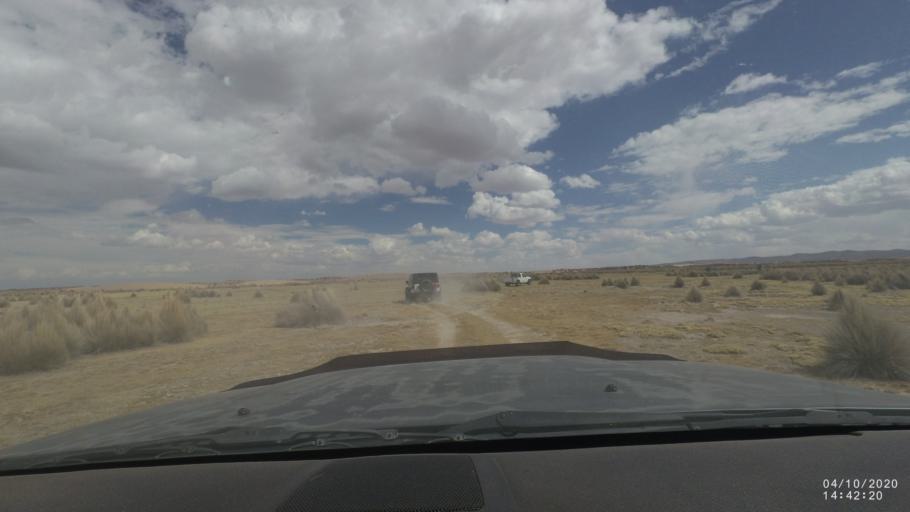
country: BO
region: Oruro
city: Poopo
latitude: -18.6860
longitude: -67.4911
